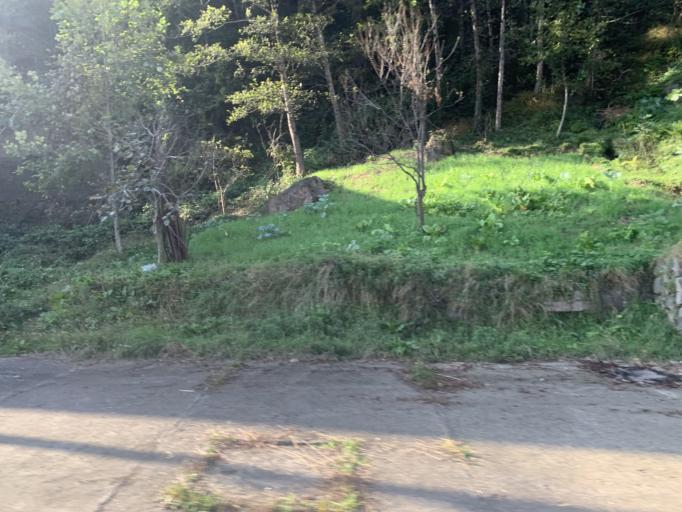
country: TR
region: Trabzon
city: Dernekpazari
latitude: 40.8417
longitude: 40.2807
